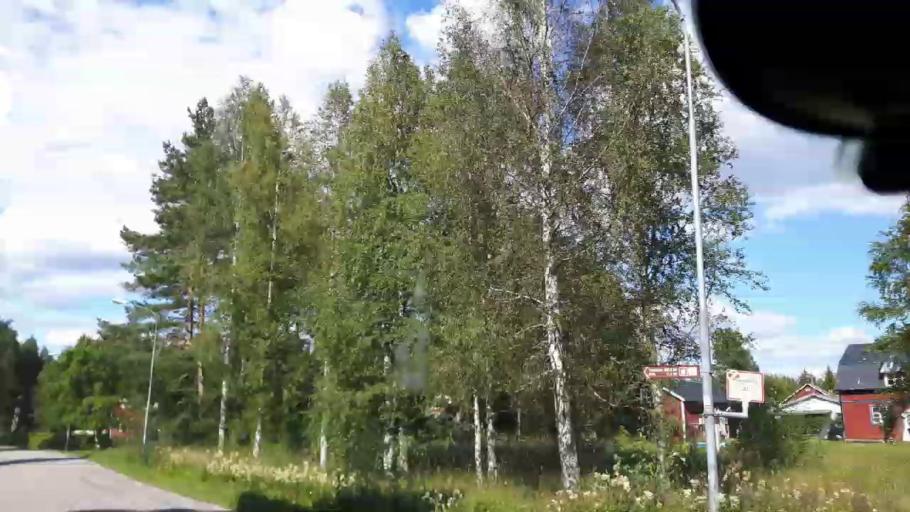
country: SE
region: Jaemtland
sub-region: Braecke Kommun
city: Braecke
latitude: 62.8321
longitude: 15.3099
